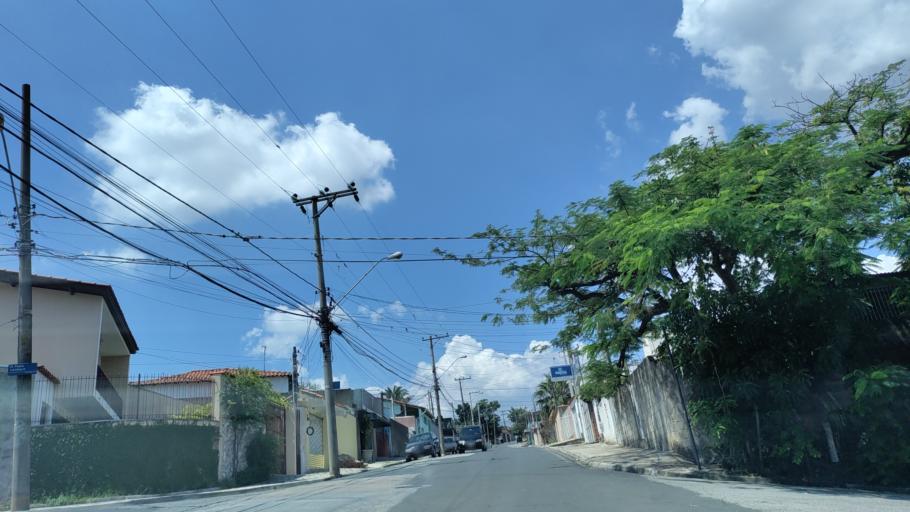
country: BR
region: Sao Paulo
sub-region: Sorocaba
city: Sorocaba
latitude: -23.4718
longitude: -47.4653
